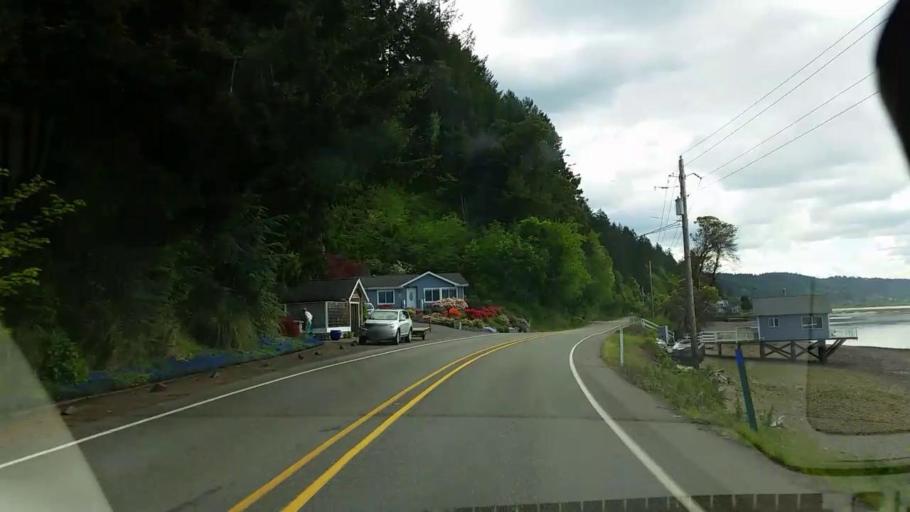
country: US
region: Washington
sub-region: Mason County
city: Shelton
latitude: 47.3527
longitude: -123.1064
